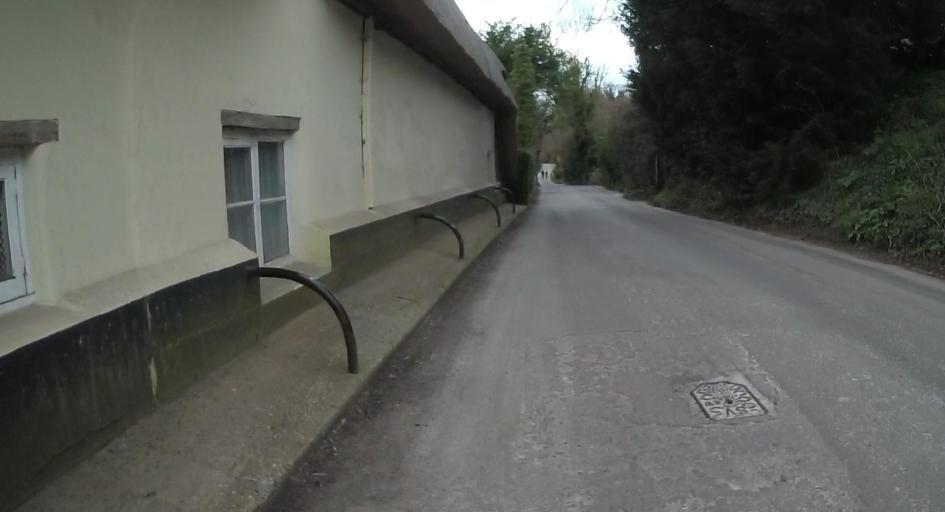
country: GB
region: England
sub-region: Hampshire
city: Andover
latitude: 51.1637
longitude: -1.4488
